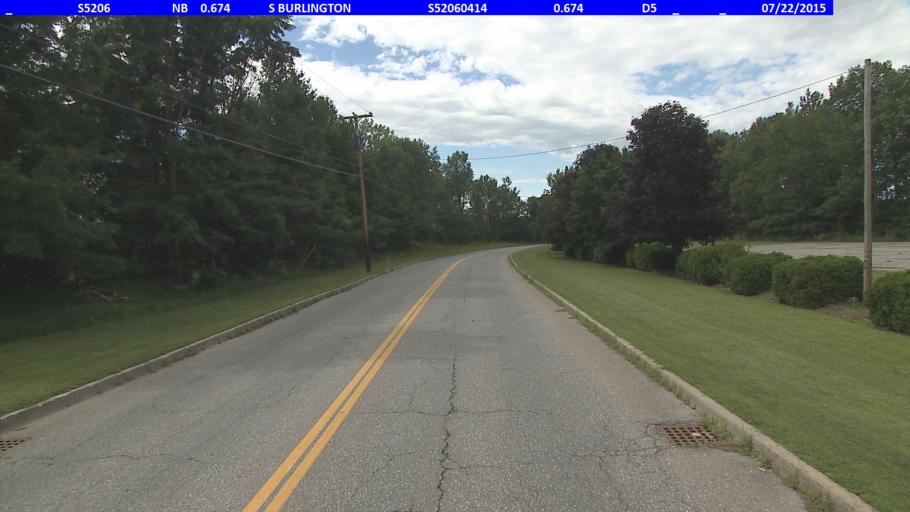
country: US
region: Vermont
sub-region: Chittenden County
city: South Burlington
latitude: 44.4789
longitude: -73.1695
